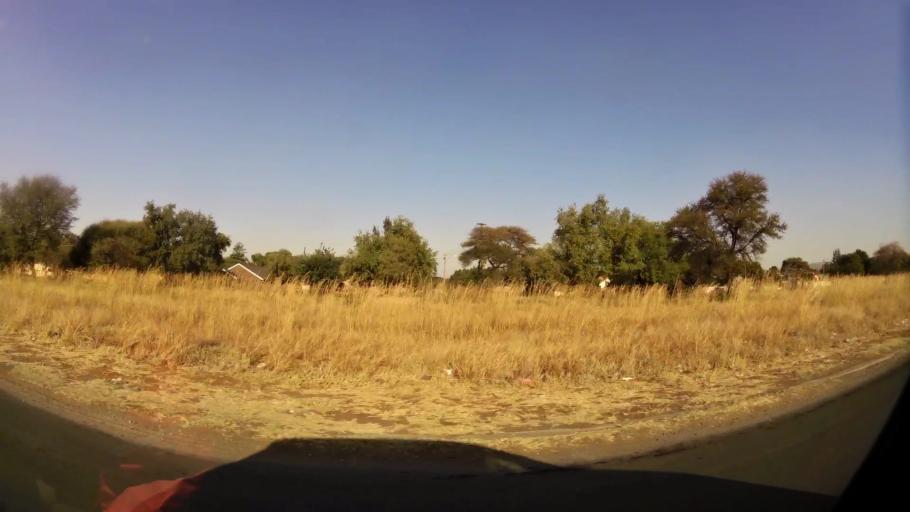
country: ZA
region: North-West
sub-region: Bojanala Platinum District Municipality
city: Rustenburg
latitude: -25.6507
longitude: 27.2233
